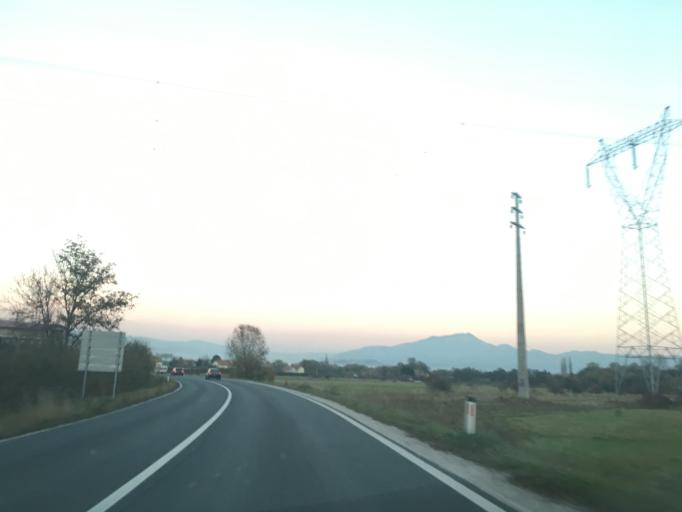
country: BA
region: Federation of Bosnia and Herzegovina
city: Hadzici
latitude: 43.8304
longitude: 18.2742
